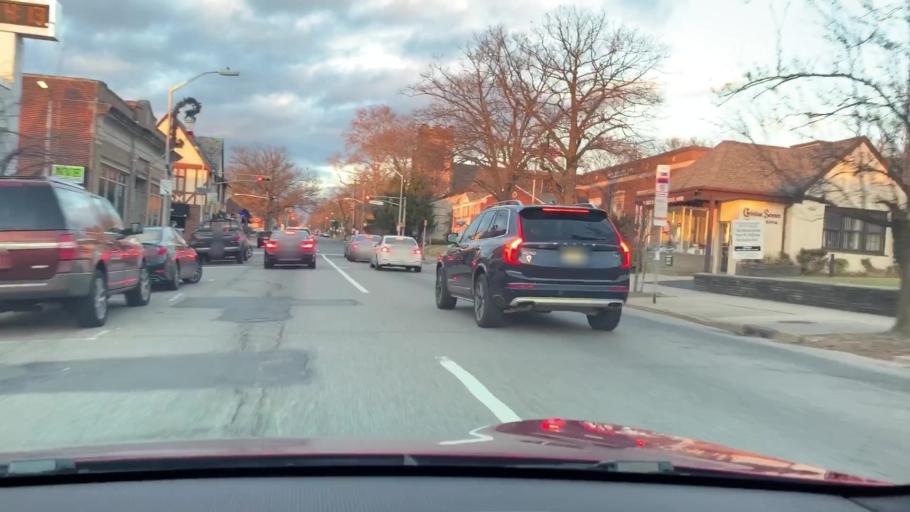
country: US
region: New Jersey
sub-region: Bergen County
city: Englewood
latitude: 40.8950
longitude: -73.9720
